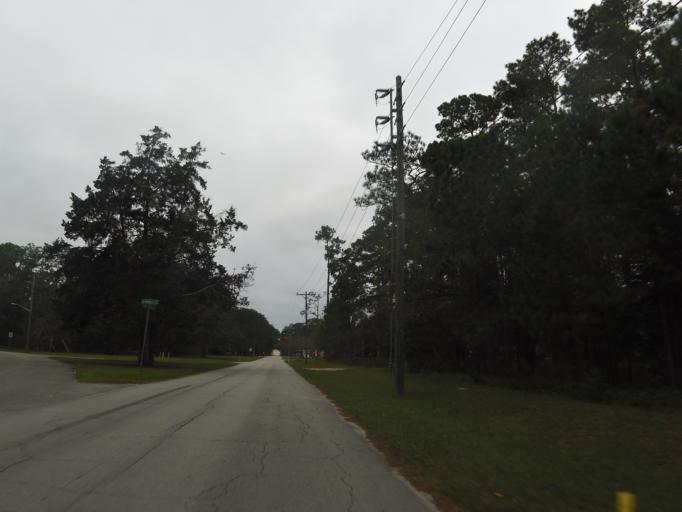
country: US
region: Florida
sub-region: Duval County
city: Baldwin
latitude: 30.2312
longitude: -81.8930
